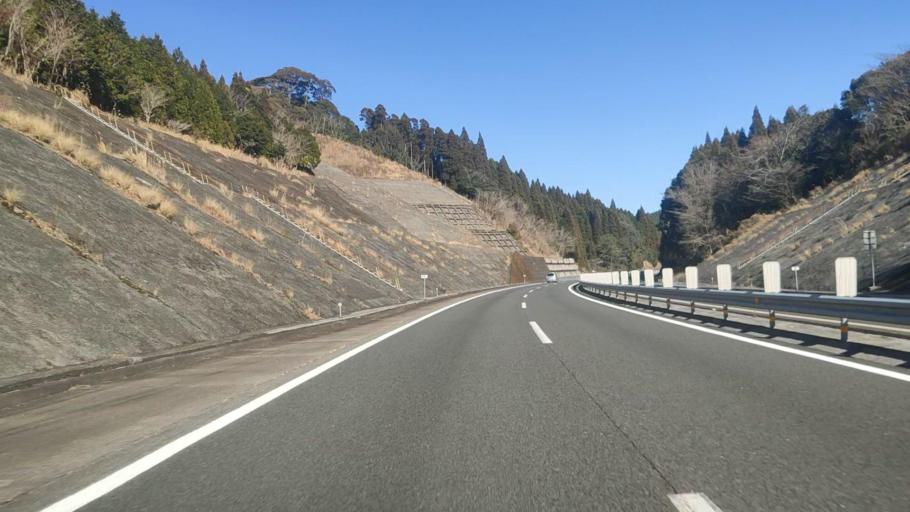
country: JP
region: Miyazaki
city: Miyakonojo
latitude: 31.8208
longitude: 131.2185
